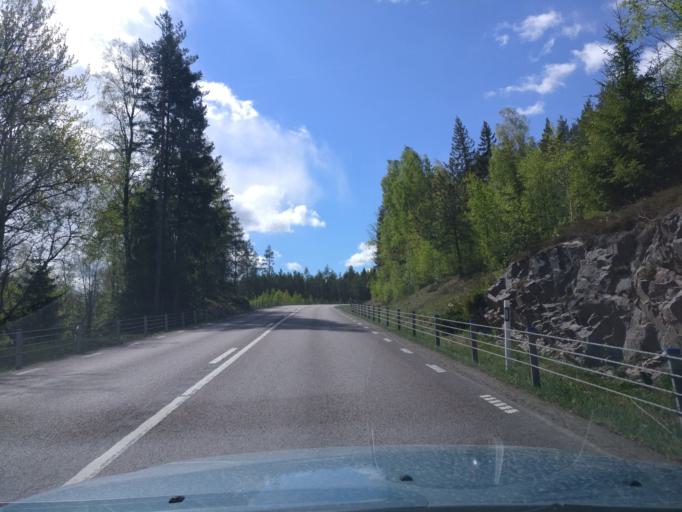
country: SE
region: Vaermland
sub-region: Karlstads Kommun
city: Molkom
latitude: 59.5866
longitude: 13.6850
